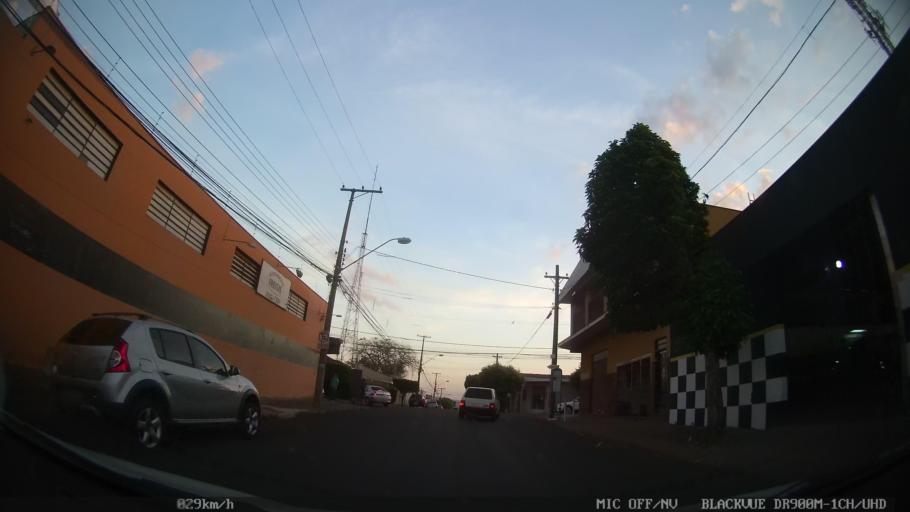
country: BR
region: Sao Paulo
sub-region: Ribeirao Preto
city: Ribeirao Preto
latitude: -21.1537
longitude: -47.8292
